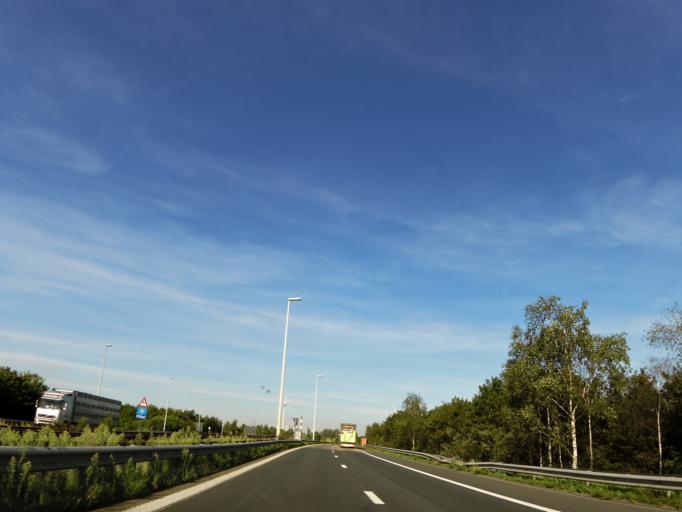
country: BE
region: Flanders
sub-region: Provincie Antwerpen
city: Stabroek
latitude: 51.3657
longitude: 4.3199
